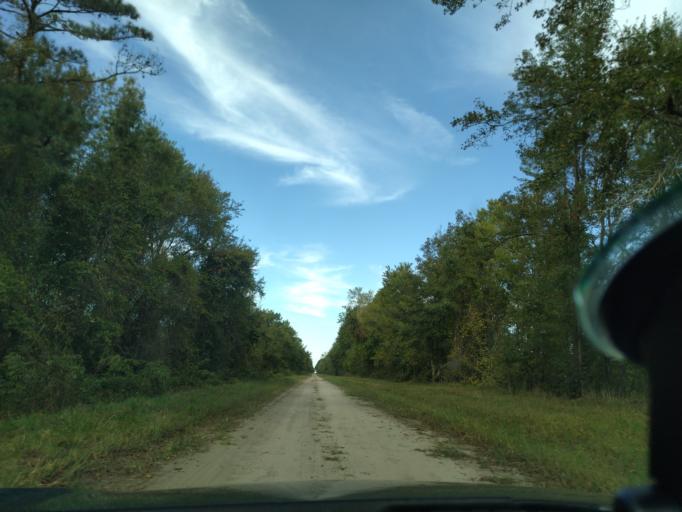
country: US
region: North Carolina
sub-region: Beaufort County
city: Belhaven
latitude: 35.7159
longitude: -76.5820
